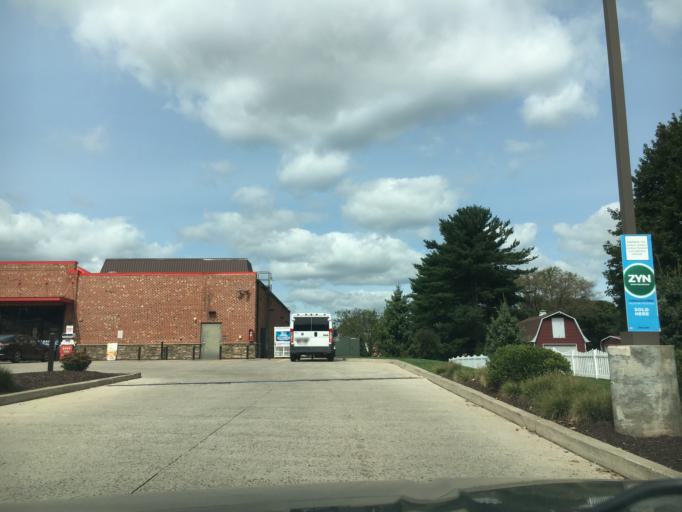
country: US
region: Pennsylvania
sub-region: Luzerne County
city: Conyngham
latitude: 40.9897
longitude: -76.0647
